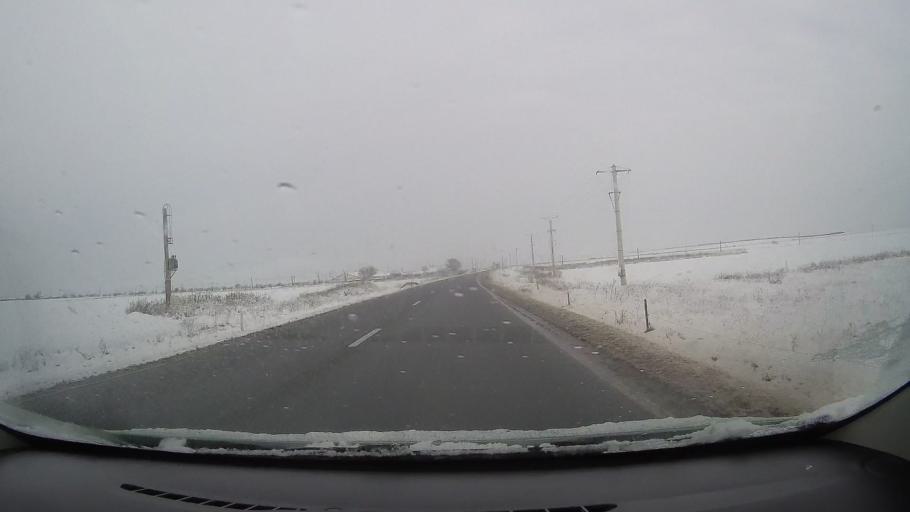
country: RO
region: Alba
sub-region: Municipiul Sebes
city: Lancram
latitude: 45.9675
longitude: 23.5294
